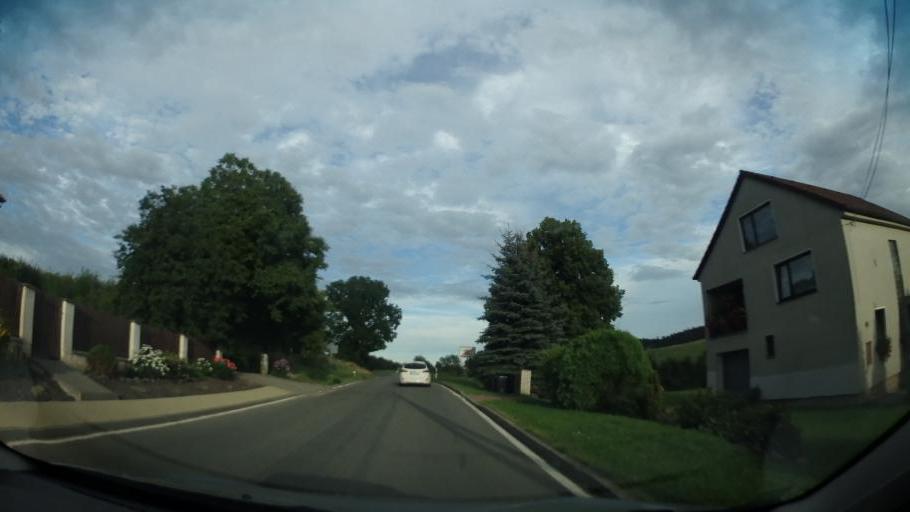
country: CZ
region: Olomoucky
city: Horni Stepanov
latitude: 49.5605
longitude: 16.7594
